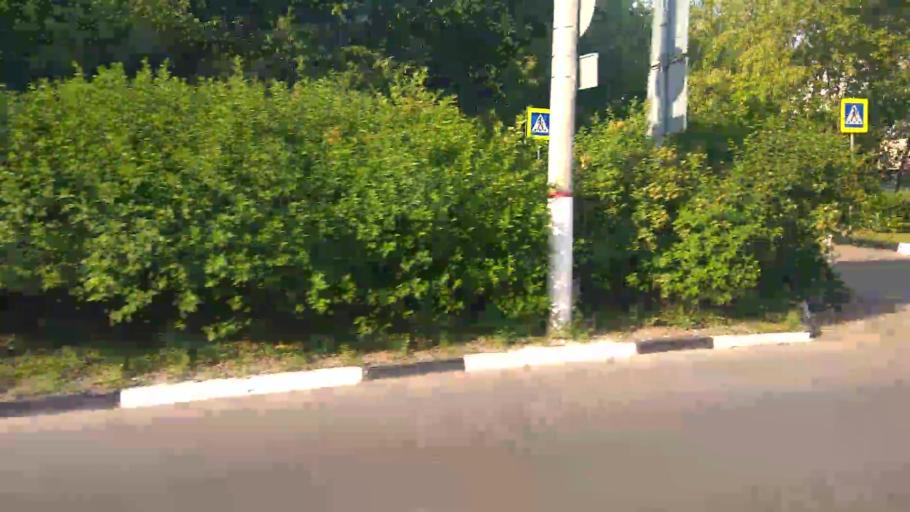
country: RU
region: Moskovskaya
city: Mytishchi
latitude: 55.9040
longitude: 37.7134
